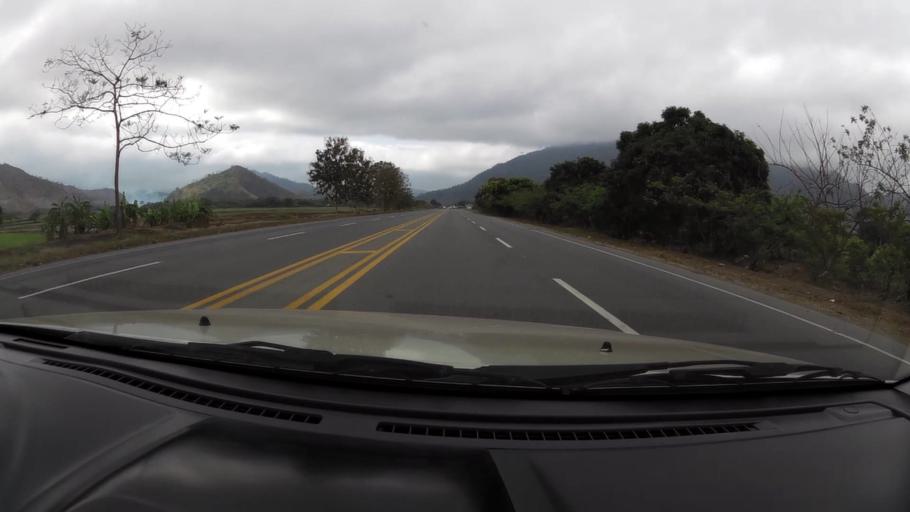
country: EC
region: Guayas
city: Coronel Marcelino Mariduena
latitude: -2.3772
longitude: -79.6317
